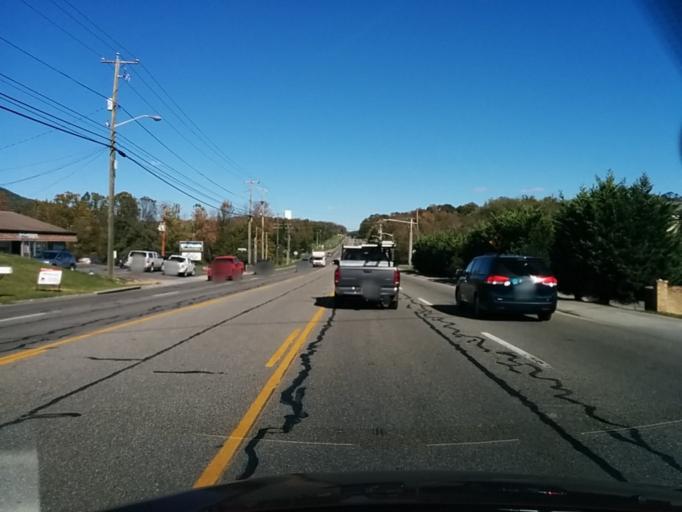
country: US
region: Virginia
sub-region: Roanoke County
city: Hollins
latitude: 37.3504
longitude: -79.9443
